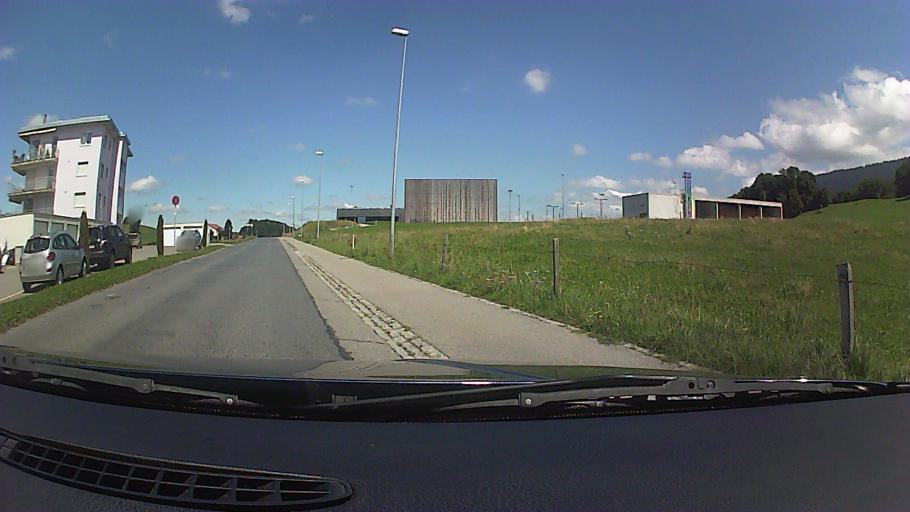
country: CH
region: Fribourg
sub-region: Veveyse District
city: Chatel-Saint-Denis
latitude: 46.5349
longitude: 6.8969
